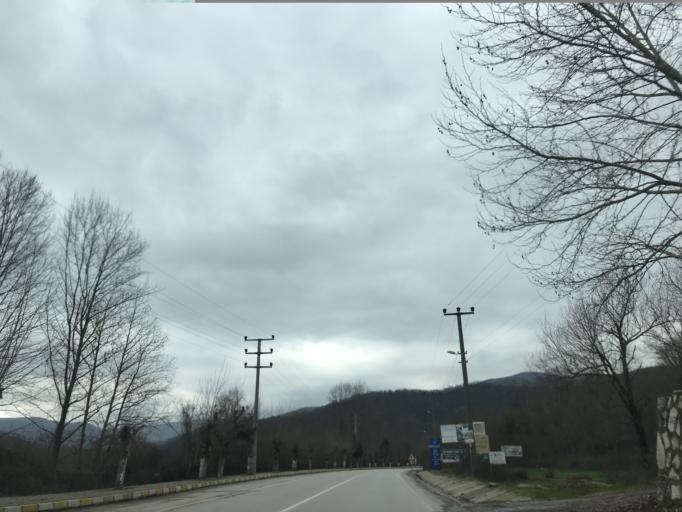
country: TR
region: Yalova
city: Termal
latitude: 40.6045
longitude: 29.1834
